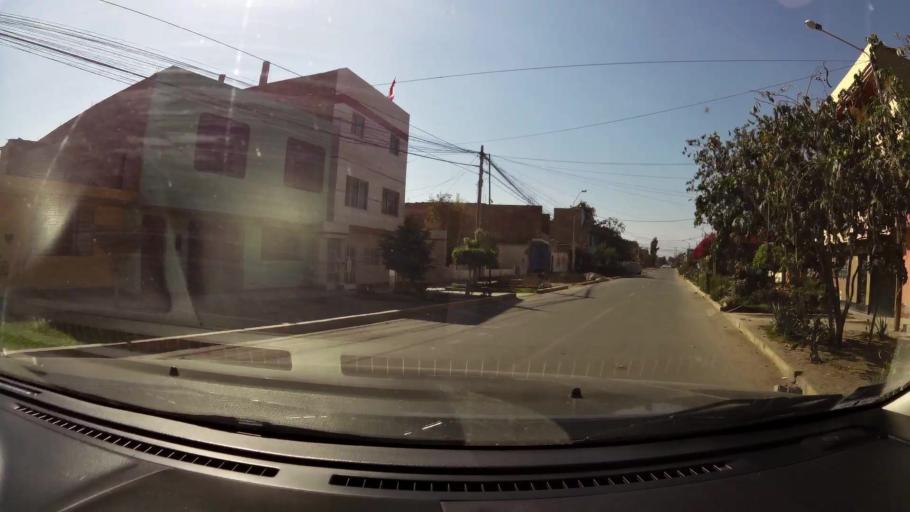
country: PE
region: Ica
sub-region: Provincia de Ica
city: La Tinguina
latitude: -14.0387
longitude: -75.7104
